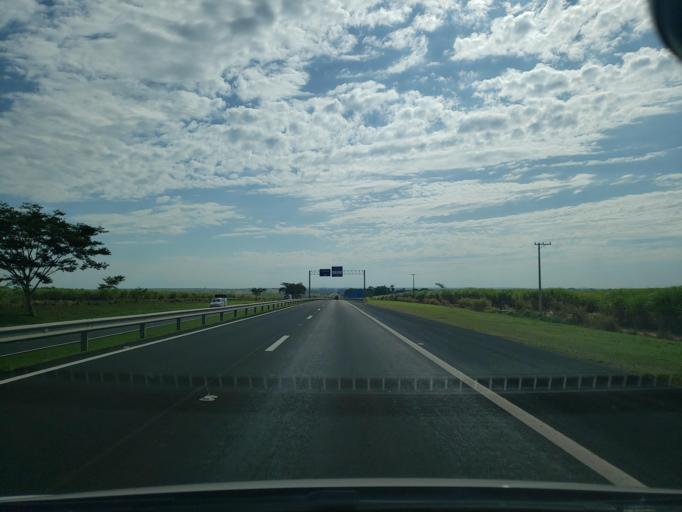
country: BR
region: Sao Paulo
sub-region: Promissao
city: Promissao
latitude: -21.6284
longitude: -49.8437
